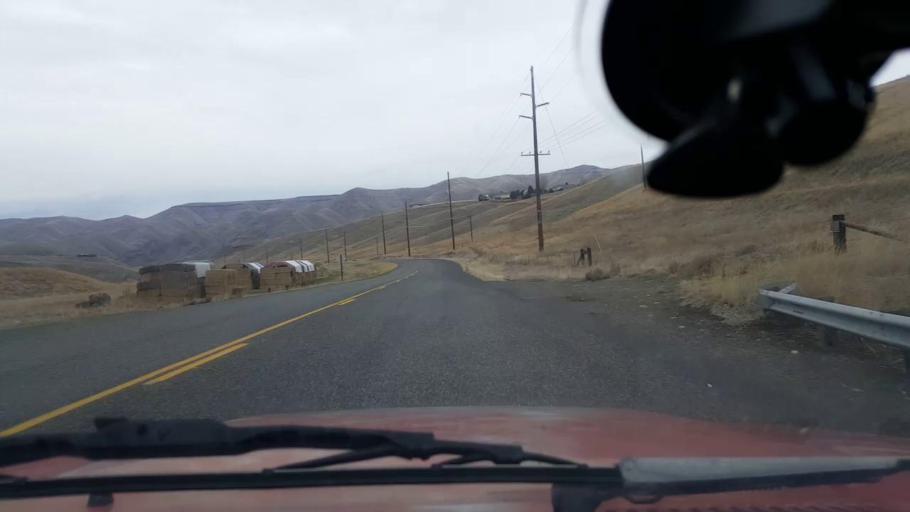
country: US
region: Washington
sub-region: Asotin County
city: Clarkston Heights-Vineland
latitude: 46.4012
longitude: -117.1013
